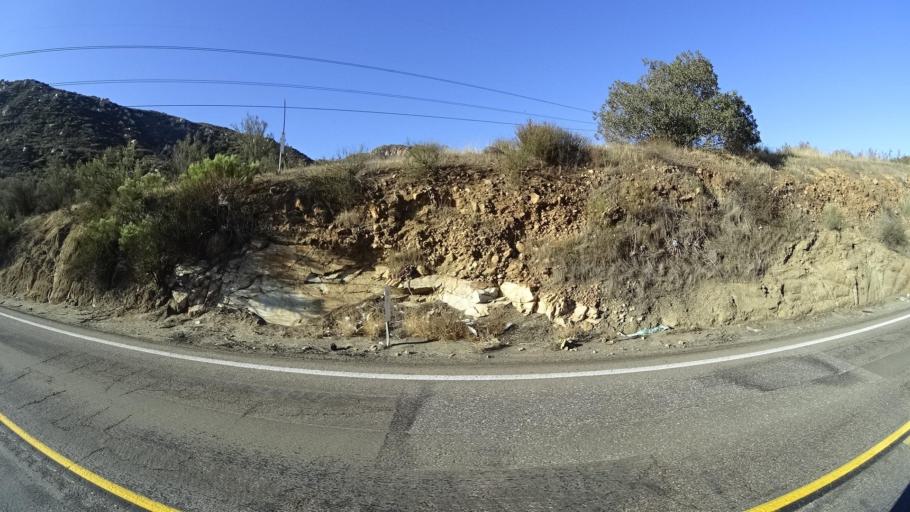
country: MX
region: Baja California
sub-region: Tecate
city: Lomas de Santa Anita
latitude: 32.6062
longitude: -116.6976
